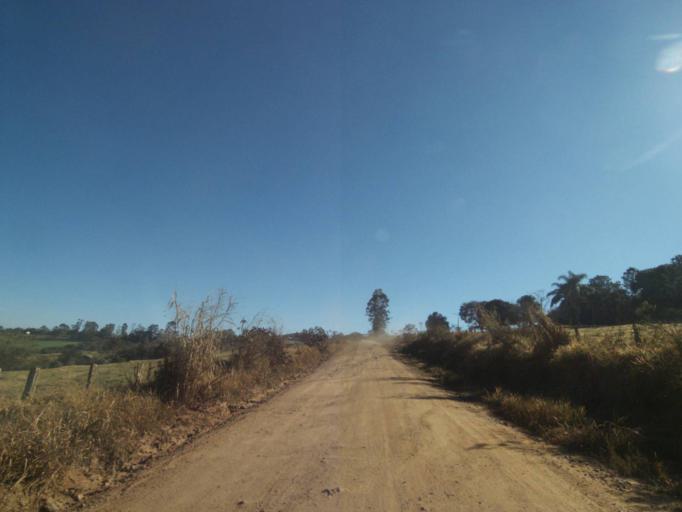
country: BR
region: Parana
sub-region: Tibagi
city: Tibagi
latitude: -24.5305
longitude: -50.3782
